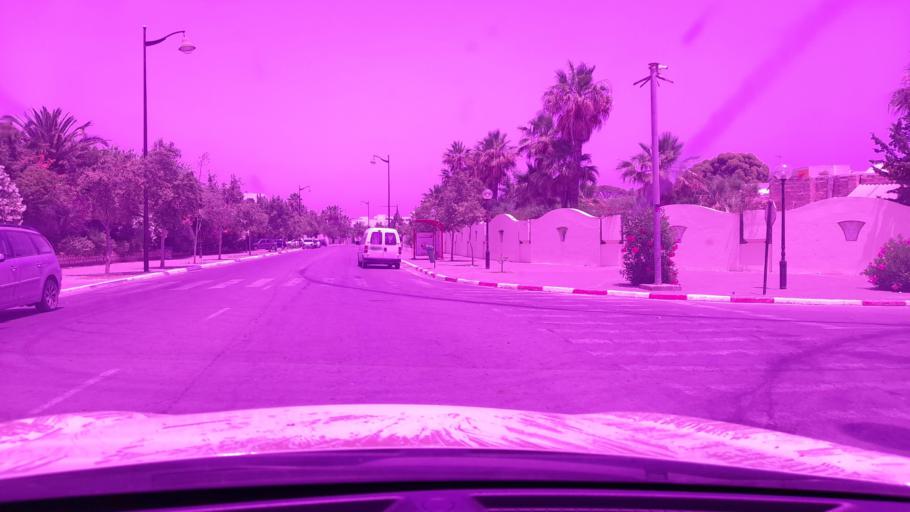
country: TN
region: Nabul
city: Al Hammamat
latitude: 36.3582
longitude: 10.5287
